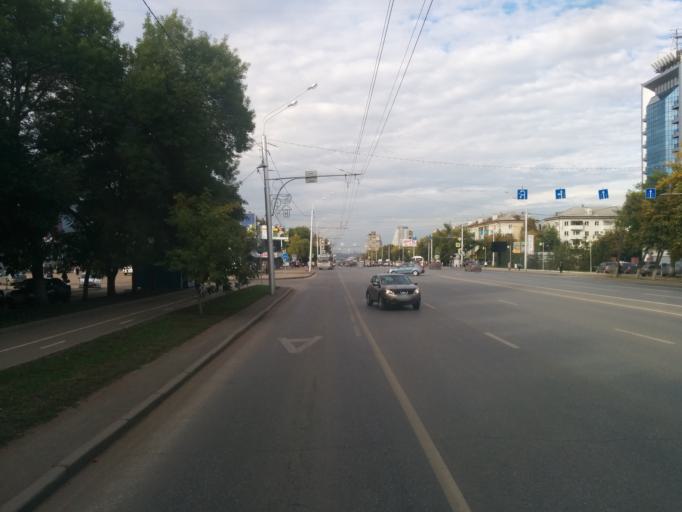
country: RU
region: Bashkortostan
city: Ufa
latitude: 54.7762
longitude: 56.0295
